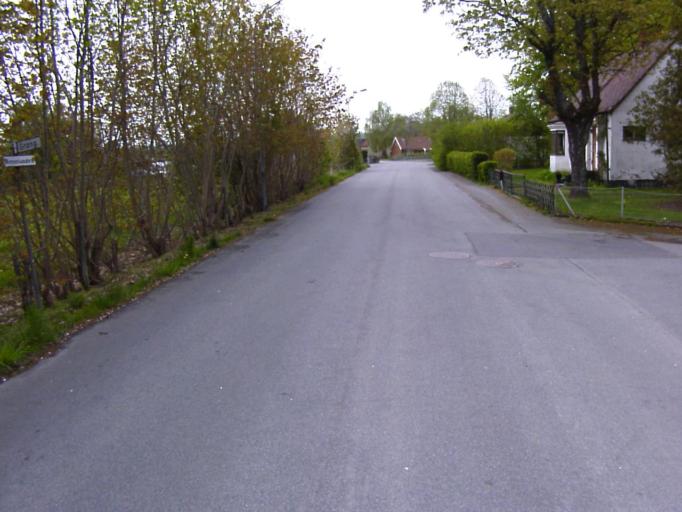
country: SE
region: Skane
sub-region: Kristianstads Kommun
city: Onnestad
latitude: 55.9346
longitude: 13.9882
